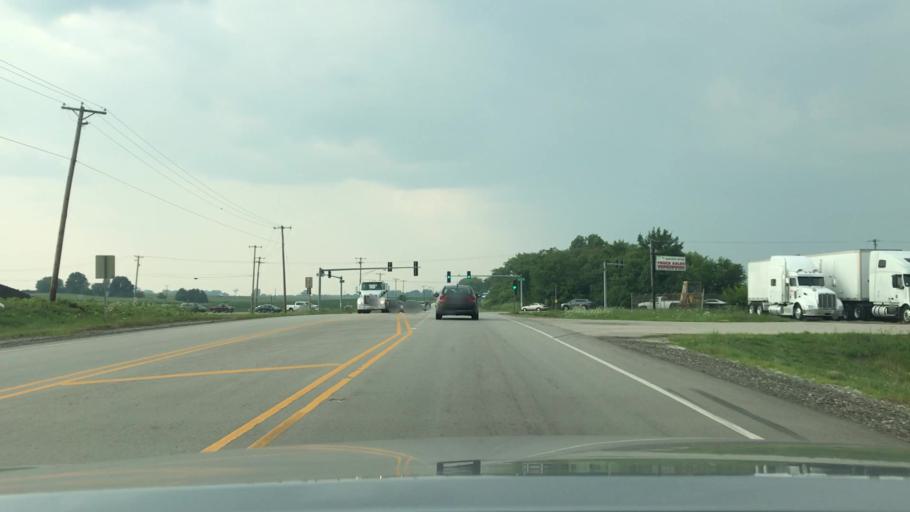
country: US
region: Illinois
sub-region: Will County
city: Plainfield
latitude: 41.6789
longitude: -88.2494
